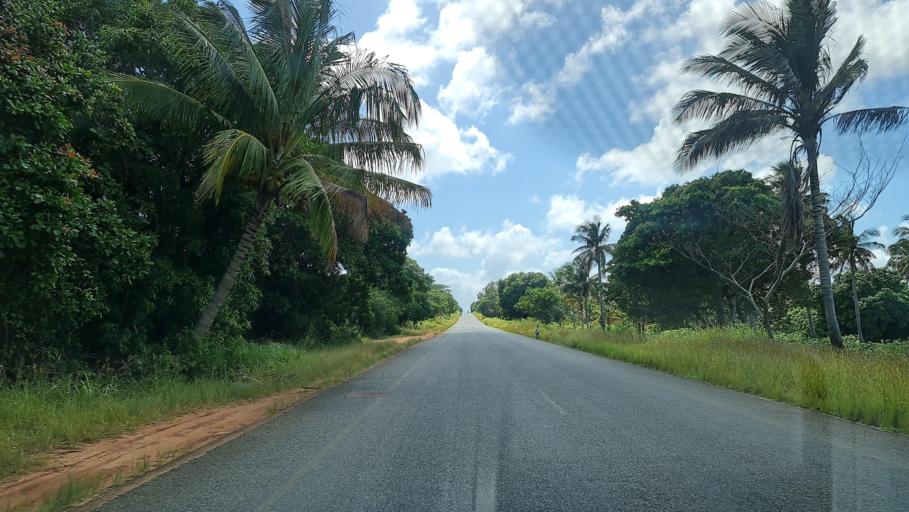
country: MZ
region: Inhambane
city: Maxixe
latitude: -24.5375
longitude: 34.9380
